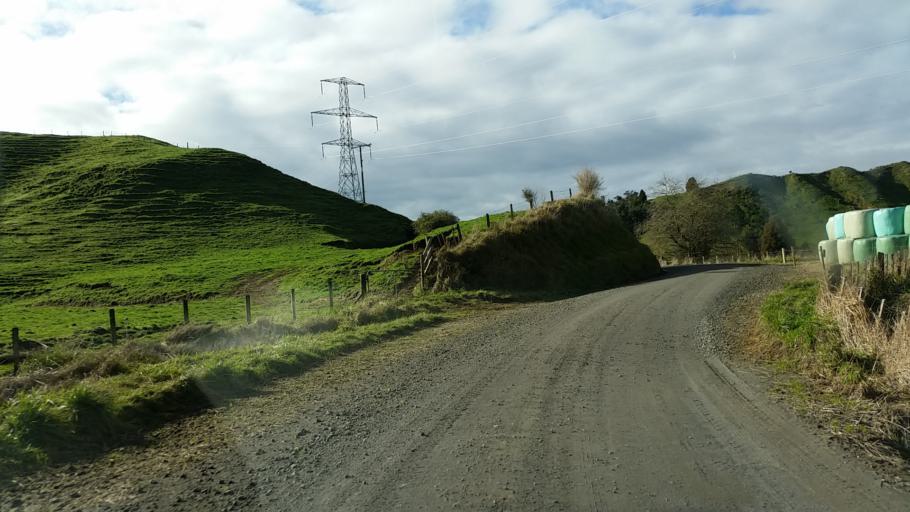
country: NZ
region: Taranaki
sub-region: South Taranaki District
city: Eltham
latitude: -39.2571
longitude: 174.5139
